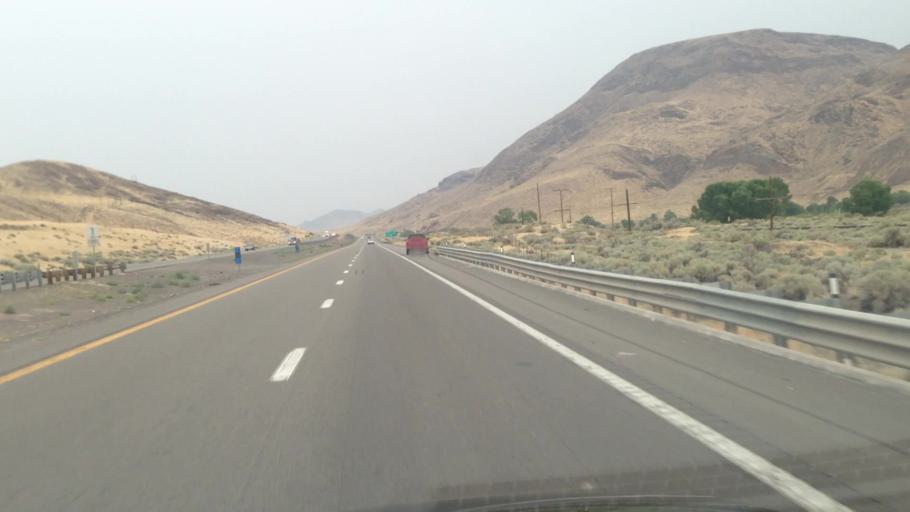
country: US
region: Nevada
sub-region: Lyon County
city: Fernley
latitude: 39.5902
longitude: -119.4540
